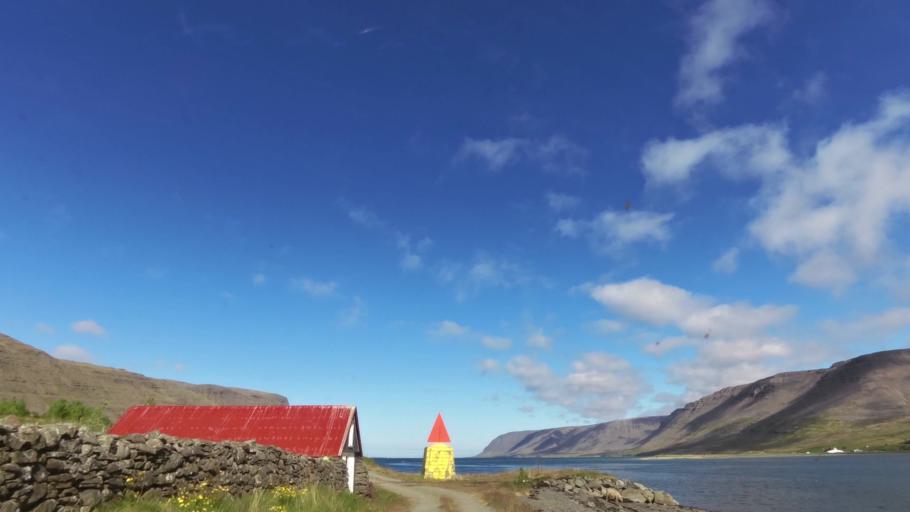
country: IS
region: West
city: Olafsvik
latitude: 65.6167
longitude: -23.8427
